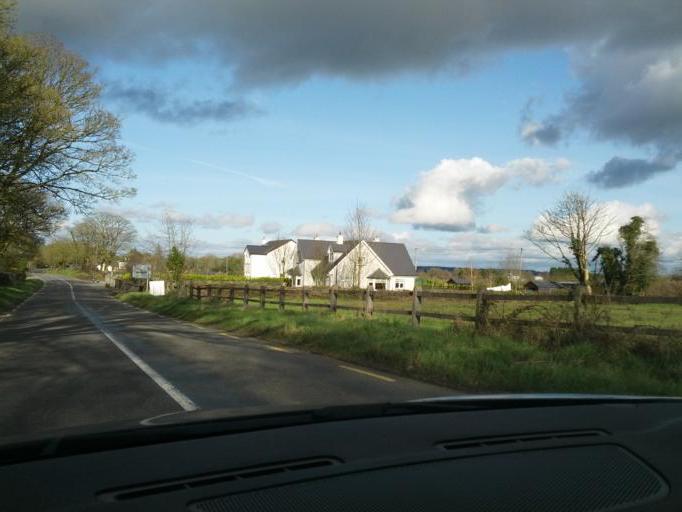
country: IE
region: Connaught
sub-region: Roscommon
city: Castlerea
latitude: 53.6893
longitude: -8.4731
